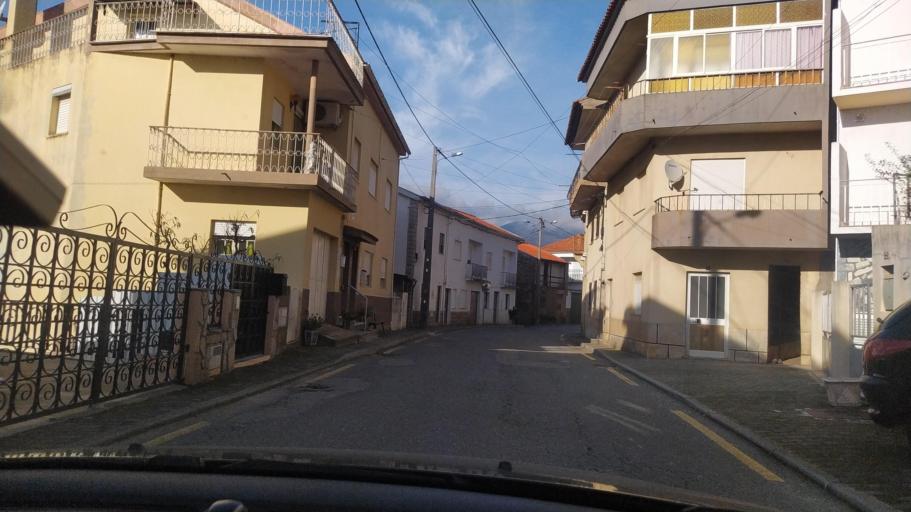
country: PT
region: Castelo Branco
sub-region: Concelho do Fundao
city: Aldeia de Joanes
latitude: 40.2009
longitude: -7.6394
